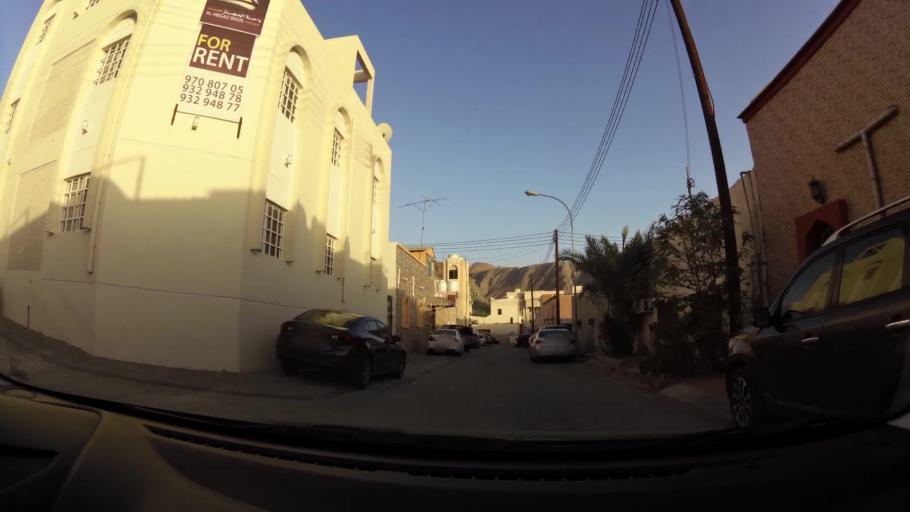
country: OM
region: Muhafazat Masqat
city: Muscat
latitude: 23.5750
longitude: 58.5737
